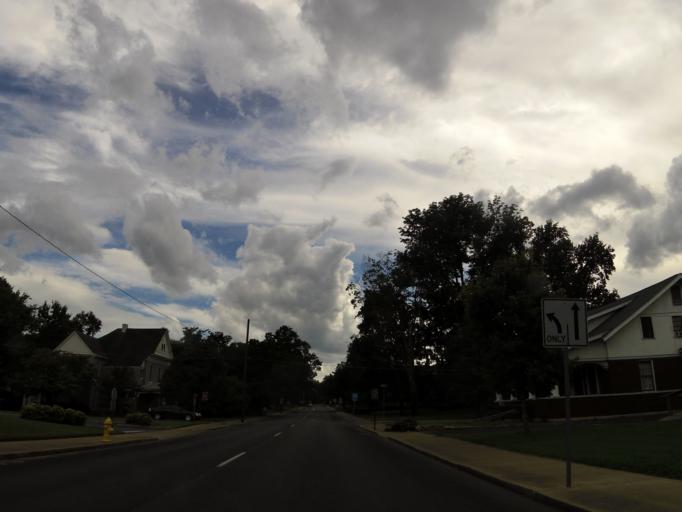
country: US
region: Kentucky
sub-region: Christian County
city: Hopkinsville
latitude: 36.8612
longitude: -87.4919
